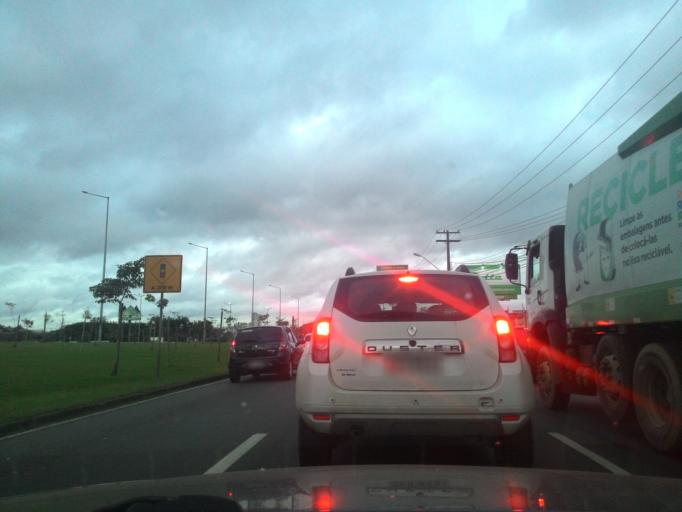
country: BR
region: Parana
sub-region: Curitiba
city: Curitiba
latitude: -25.4724
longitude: -49.2561
